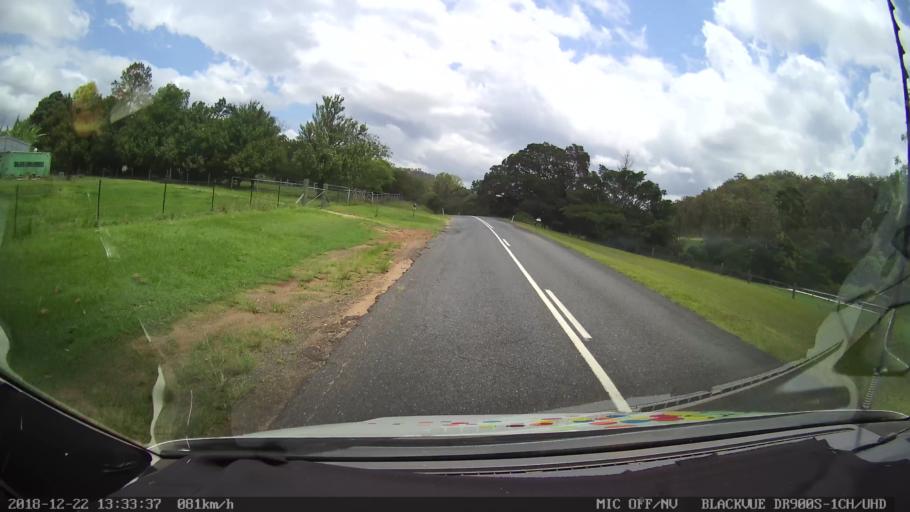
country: AU
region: New South Wales
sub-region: Clarence Valley
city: Coutts Crossing
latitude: -29.8637
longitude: 152.8252
